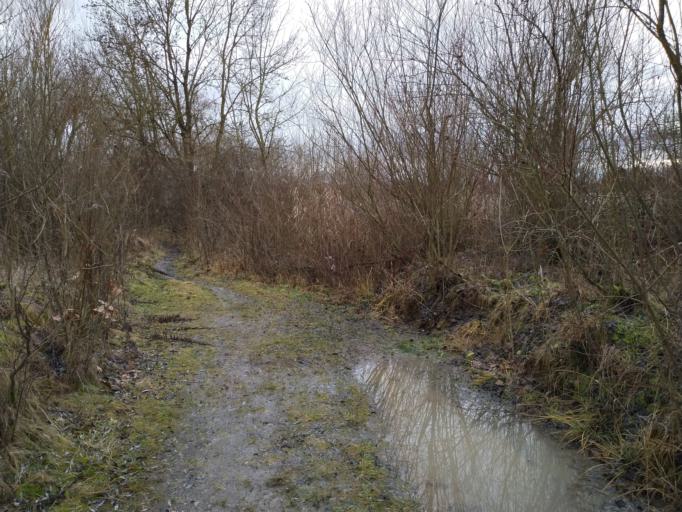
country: DE
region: Bavaria
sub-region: Swabia
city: Bachingen an der Brenz
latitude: 48.5011
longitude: 10.2999
